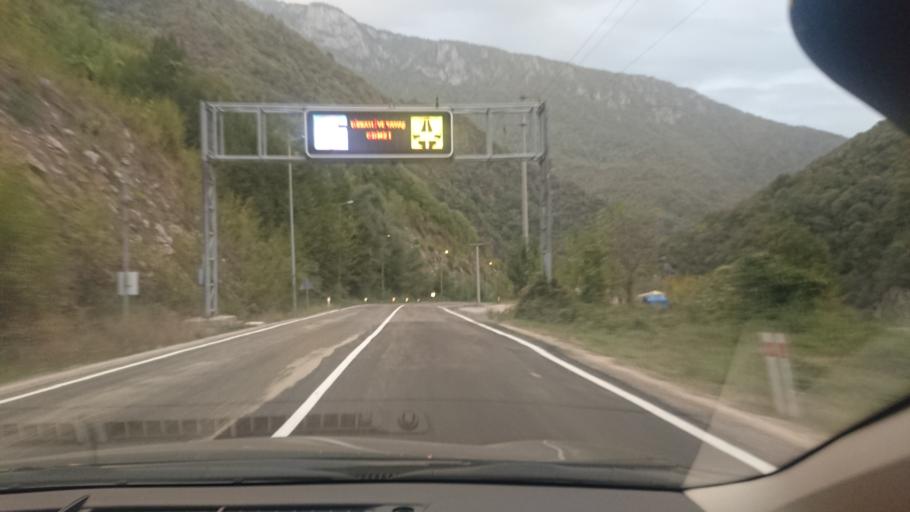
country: TR
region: Karabuk
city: Yenice
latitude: 41.1573
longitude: 32.4664
